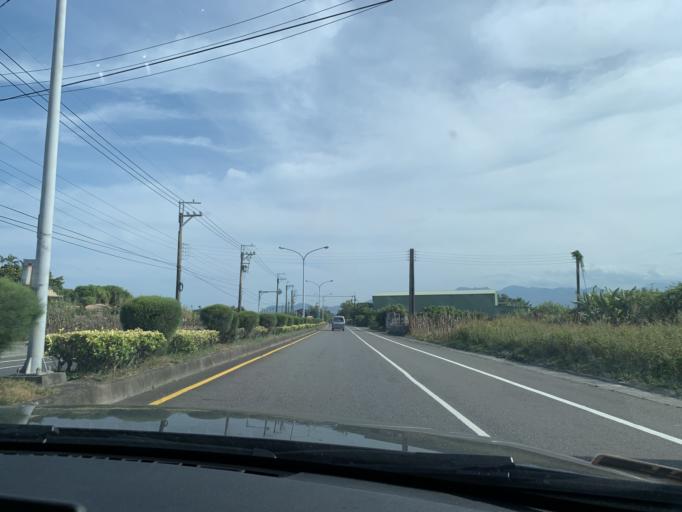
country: TW
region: Taiwan
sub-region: Yilan
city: Yilan
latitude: 24.7420
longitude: 121.8166
